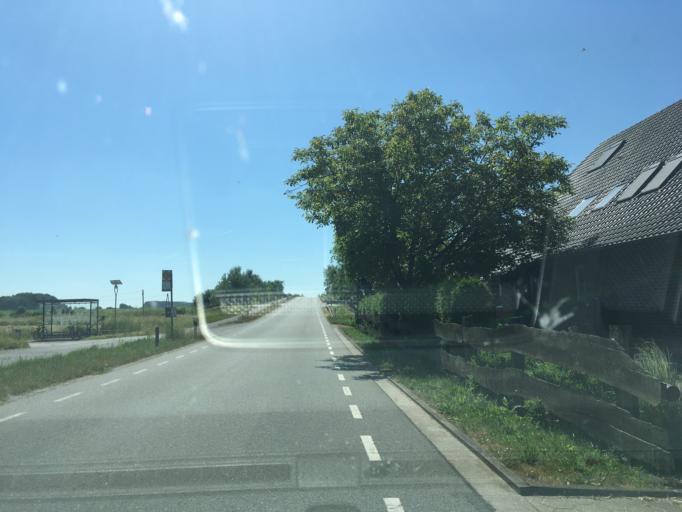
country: DE
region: North Rhine-Westphalia
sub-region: Regierungsbezirk Munster
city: Borken
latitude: 51.8279
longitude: 6.7972
